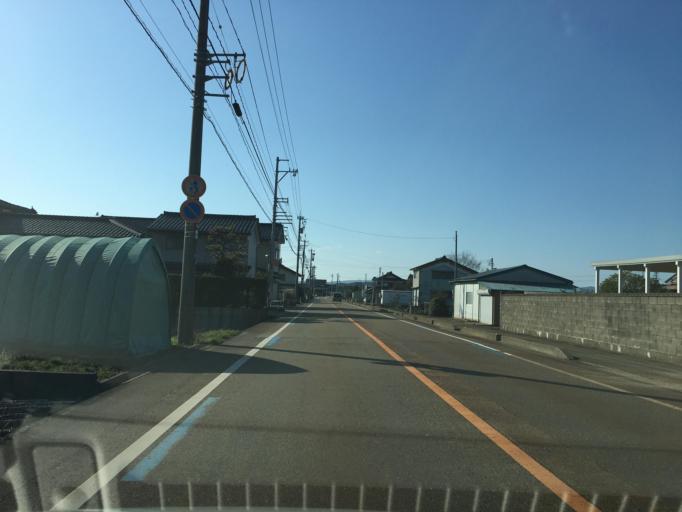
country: JP
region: Toyama
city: Himi
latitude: 36.8268
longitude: 137.0068
